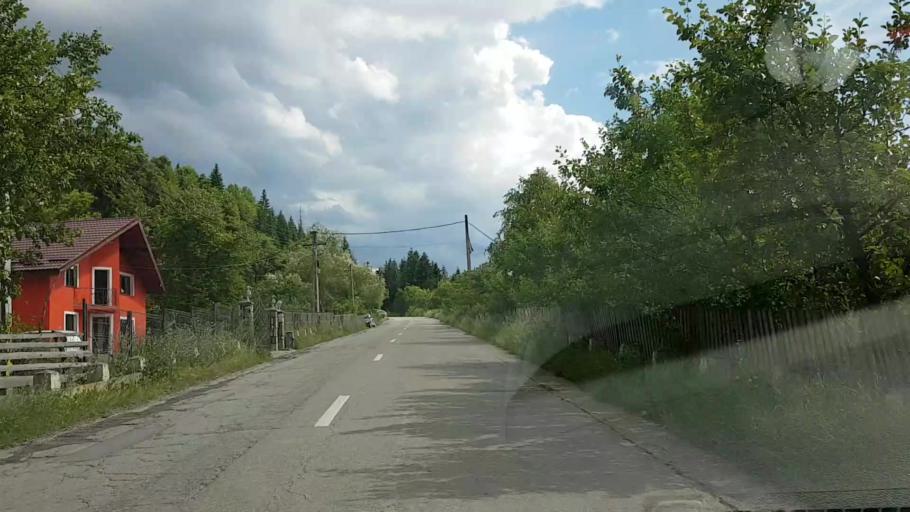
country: RO
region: Neamt
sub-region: Comuna Hangu
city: Hangu
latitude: 47.0569
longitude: 26.0375
